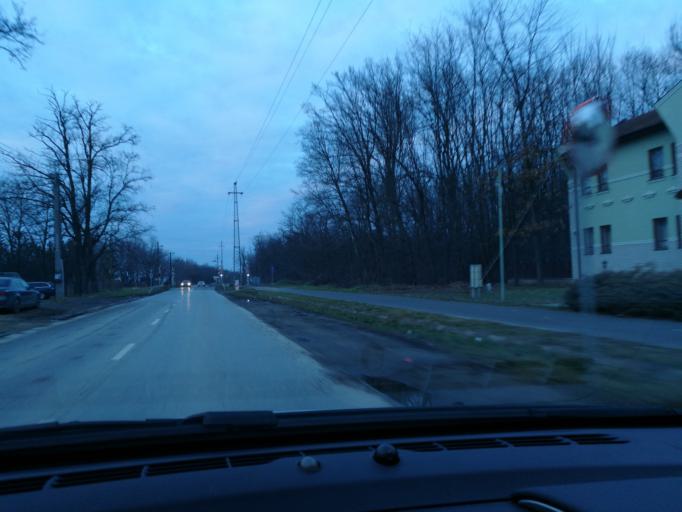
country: HU
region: Szabolcs-Szatmar-Bereg
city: Nyiregyhaza
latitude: 47.9756
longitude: 21.7062
